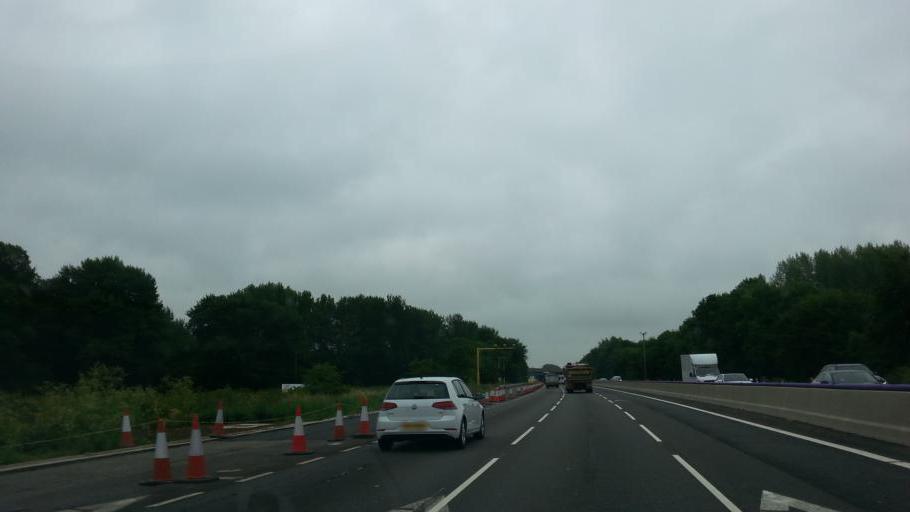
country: GB
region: England
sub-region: Northamptonshire
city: Long Buckby
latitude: 52.2621
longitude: -1.0879
